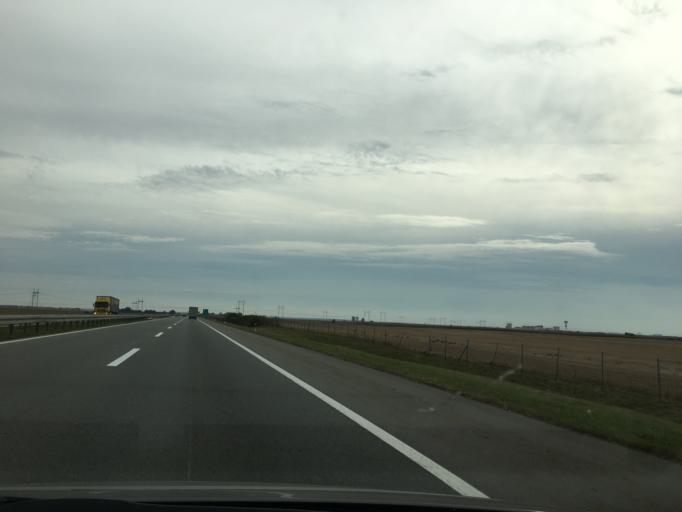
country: RS
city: Novi Karlovci
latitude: 45.0845
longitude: 20.1329
